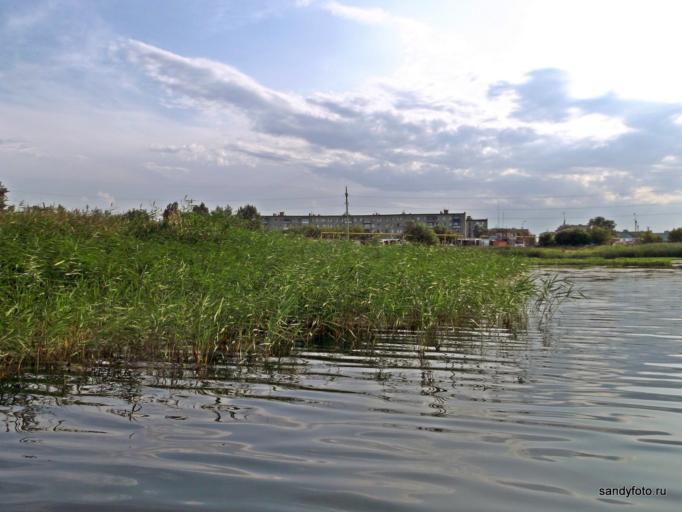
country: RU
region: Chelyabinsk
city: Troitsk
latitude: 54.0935
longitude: 61.5594
